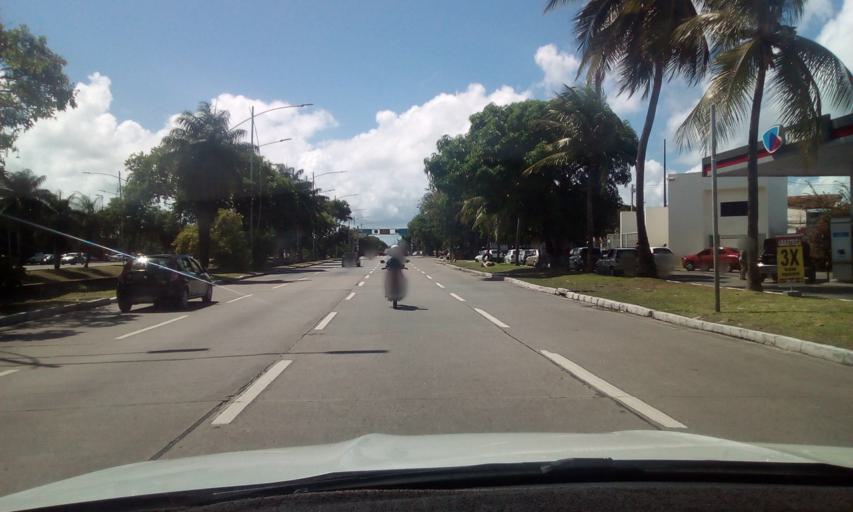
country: BR
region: Pernambuco
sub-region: Recife
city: Recife
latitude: -8.0407
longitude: -34.8803
